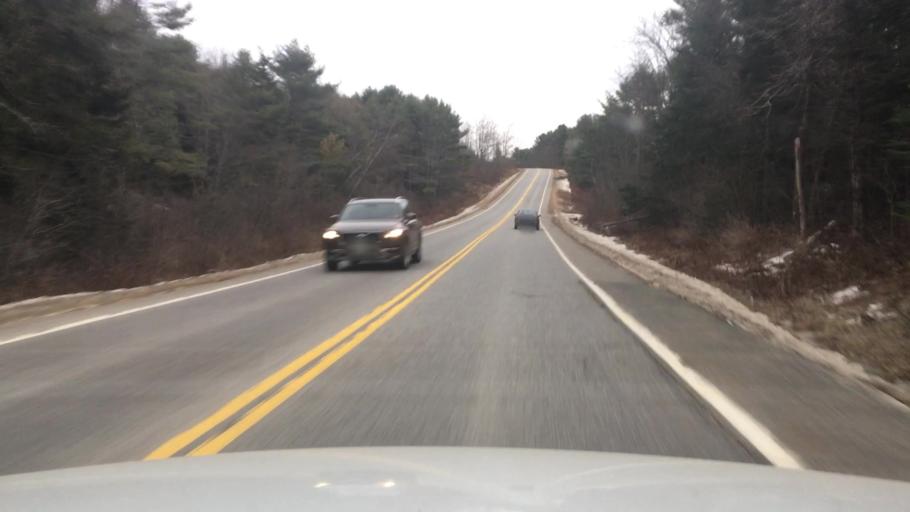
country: US
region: Maine
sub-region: Sagadahoc County
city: Topsham
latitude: 43.8877
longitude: -70.0191
